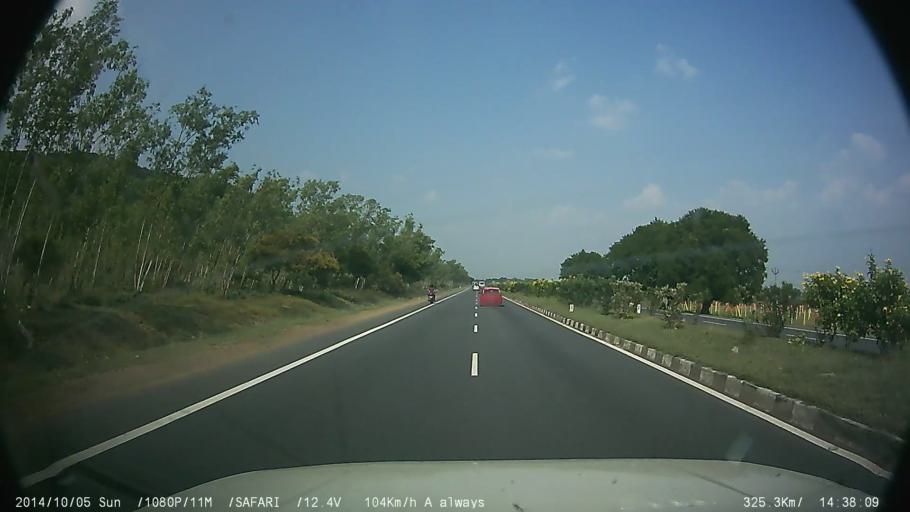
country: IN
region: Tamil Nadu
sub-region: Kancheepuram
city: Madurantakam
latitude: 12.3848
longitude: 79.7946
